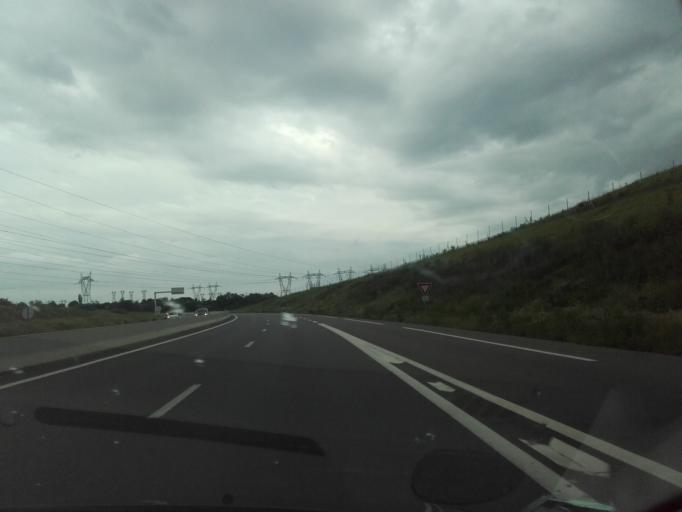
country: FR
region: Rhone-Alpes
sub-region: Departement du Rhone
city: Lentilly
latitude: 45.8242
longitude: 4.6862
